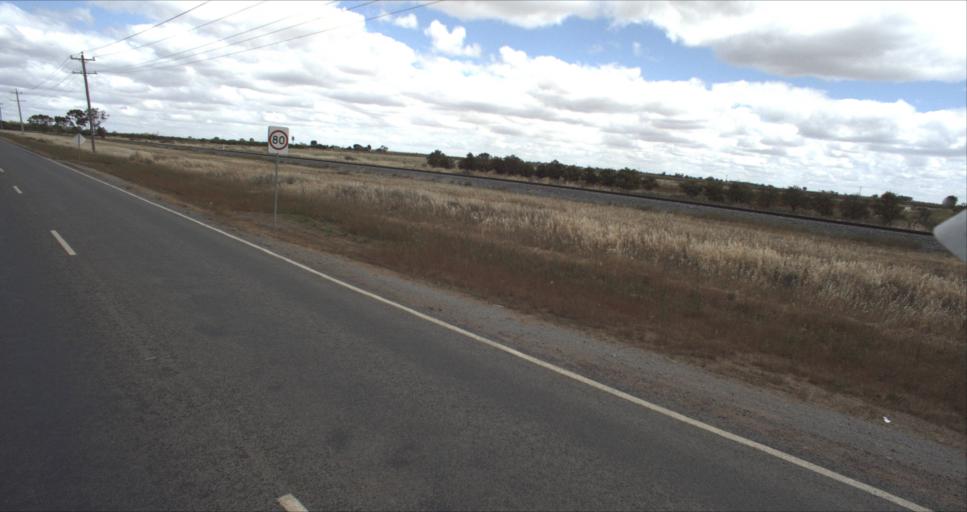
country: AU
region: New South Wales
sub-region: Leeton
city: Leeton
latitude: -34.5730
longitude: 146.3947
